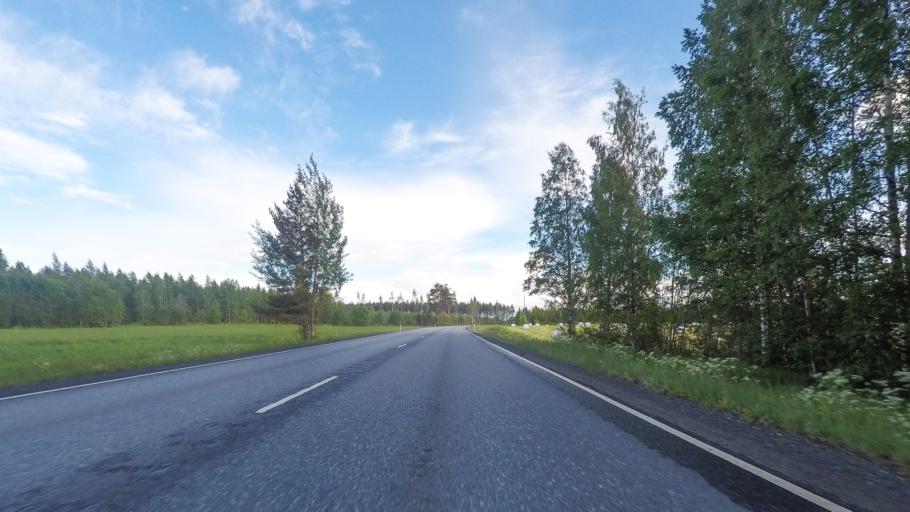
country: FI
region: Central Finland
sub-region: Joutsa
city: Joutsa
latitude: 61.6950
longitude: 26.0582
